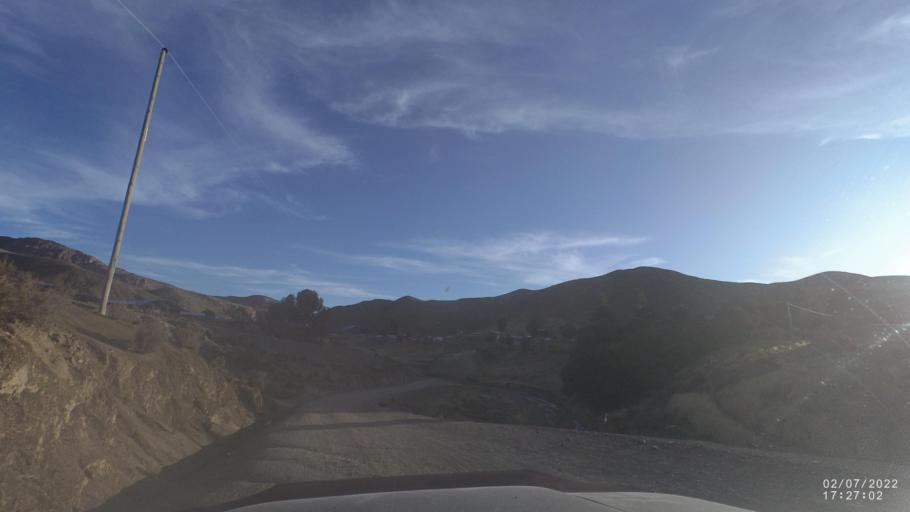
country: BO
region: Cochabamba
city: Irpa Irpa
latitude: -17.8822
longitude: -66.6146
